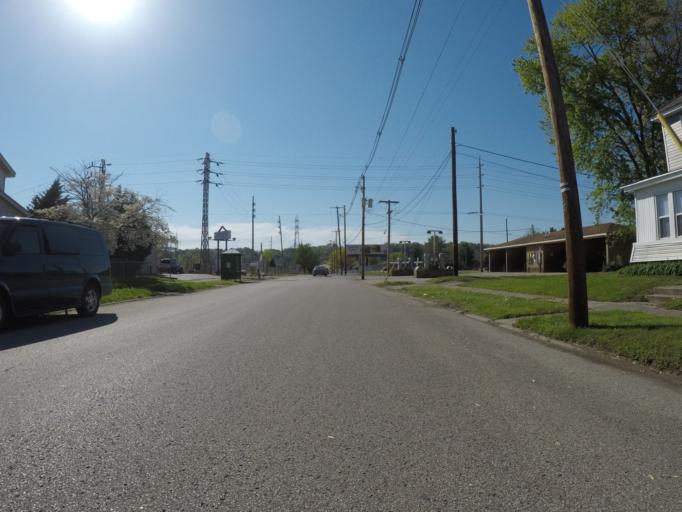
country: US
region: West Virginia
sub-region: Wayne County
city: Kenova
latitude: 38.4022
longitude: -82.5875
